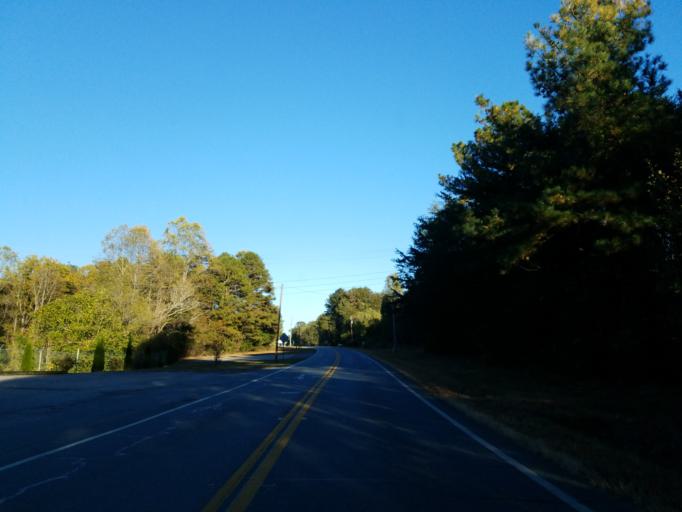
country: US
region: Georgia
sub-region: Dawson County
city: Dawsonville
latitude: 34.4210
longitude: -84.1341
